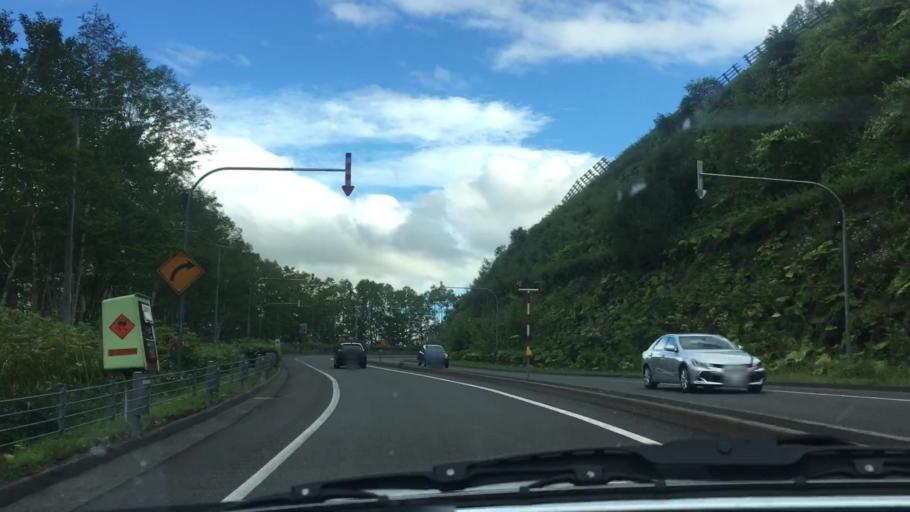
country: JP
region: Hokkaido
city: Shimo-furano
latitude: 43.1493
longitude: 142.7733
